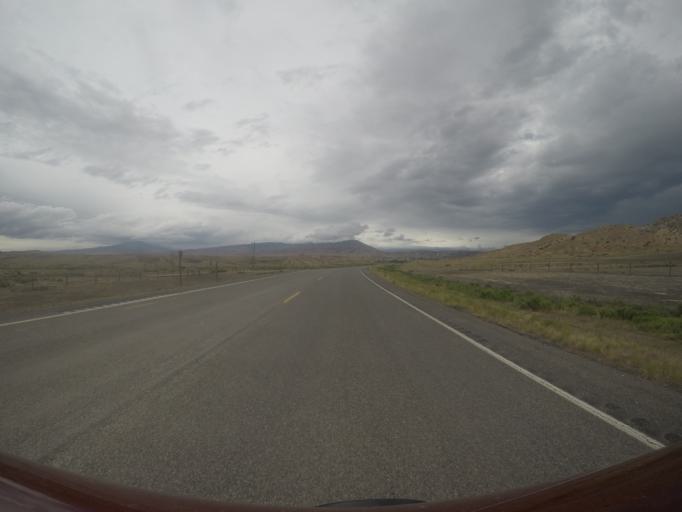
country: US
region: Wyoming
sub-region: Big Horn County
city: Lovell
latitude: 44.9484
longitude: -108.2970
